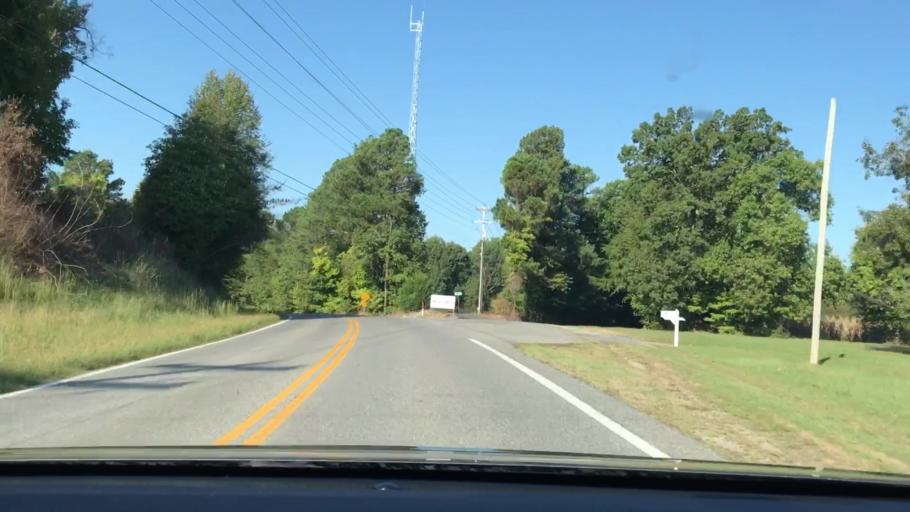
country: US
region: Kentucky
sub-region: Marshall County
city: Benton
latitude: 36.7659
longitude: -88.2664
